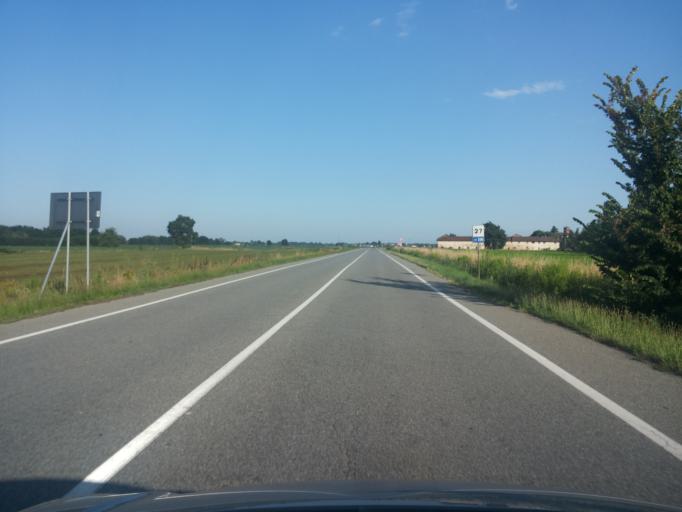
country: IT
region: Piedmont
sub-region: Provincia di Vercelli
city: Villarboit
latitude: 45.4122
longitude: 8.3220
